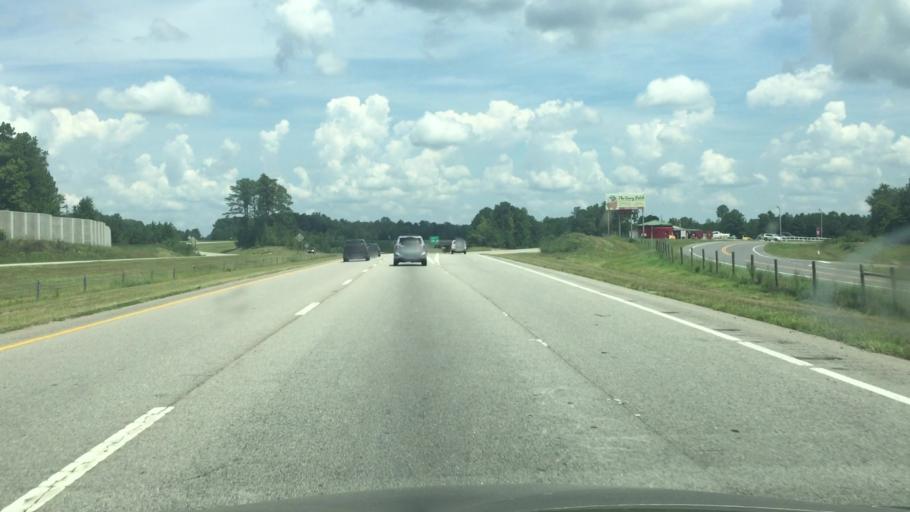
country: US
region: North Carolina
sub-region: Richmond County
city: Ellerbe
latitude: 35.0390
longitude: -79.7684
